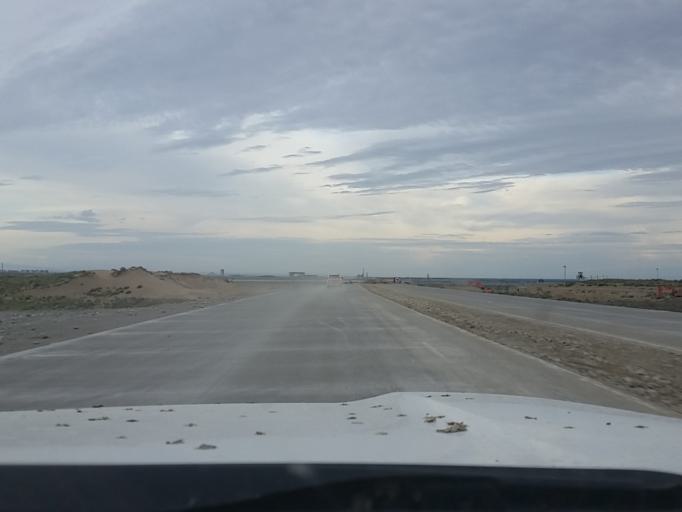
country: KZ
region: Almaty Oblysy
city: Zharkent
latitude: 44.1730
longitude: 80.3432
